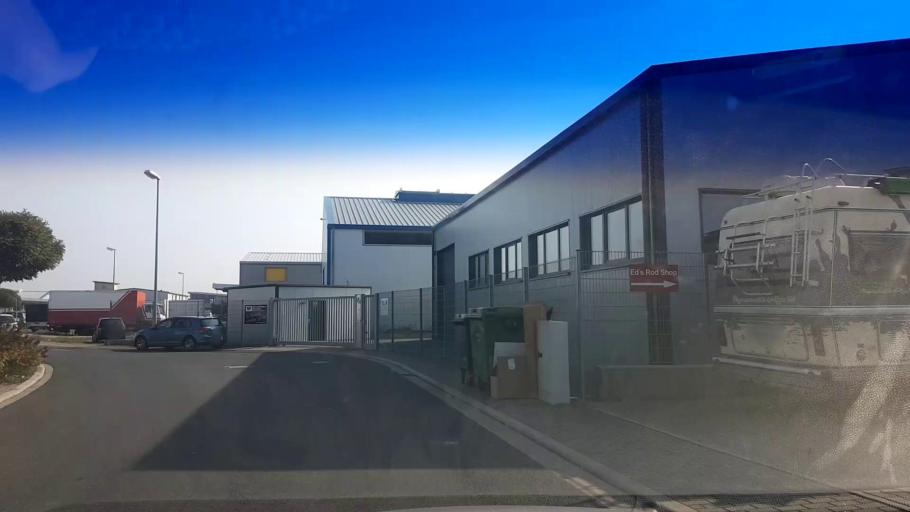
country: DE
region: Bavaria
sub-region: Upper Franconia
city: Viereth-Trunstadt
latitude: 49.9365
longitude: 10.7804
